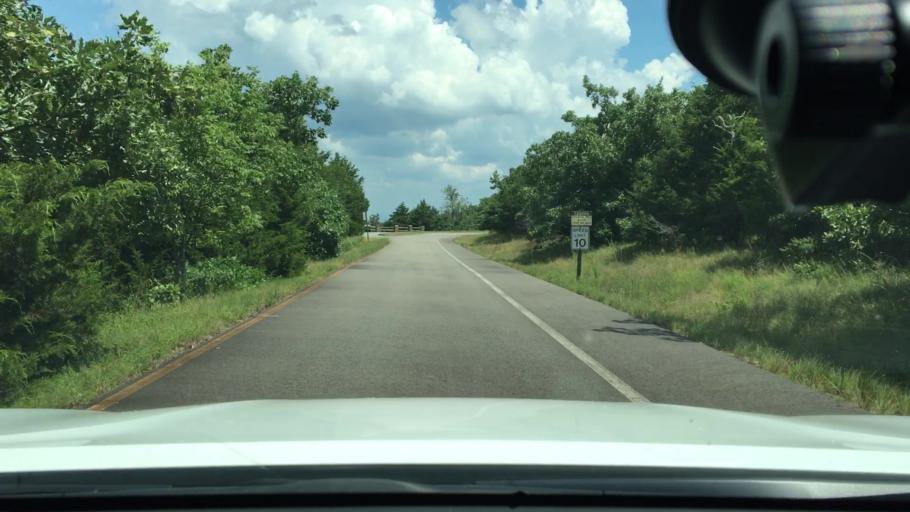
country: US
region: Arkansas
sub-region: Logan County
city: Paris
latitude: 35.1714
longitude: -93.6476
